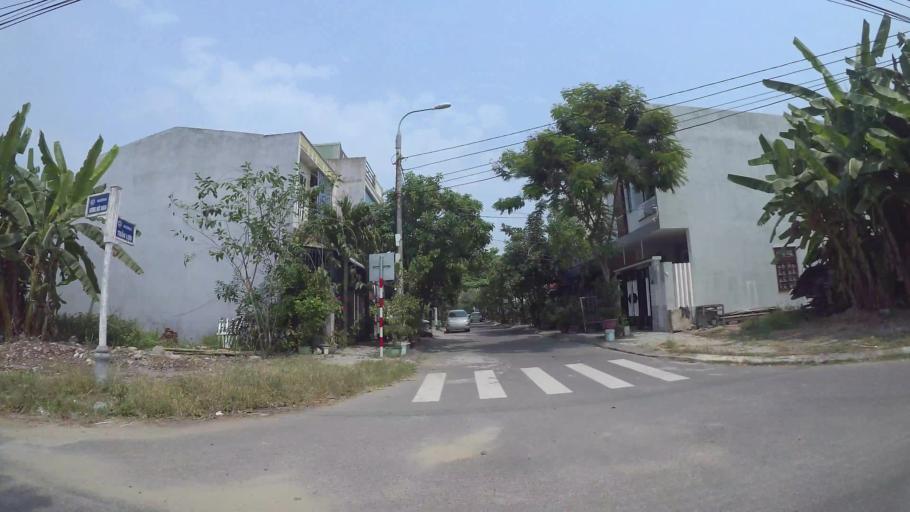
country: VN
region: Da Nang
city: Cam Le
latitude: 15.9989
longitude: 108.2127
